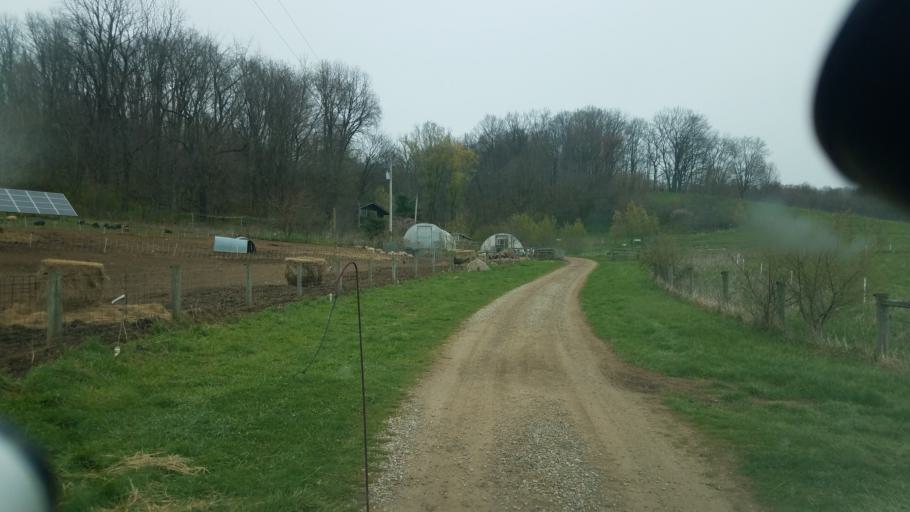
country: US
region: Ohio
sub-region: Knox County
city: Fredericktown
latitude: 40.5279
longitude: -82.4640
